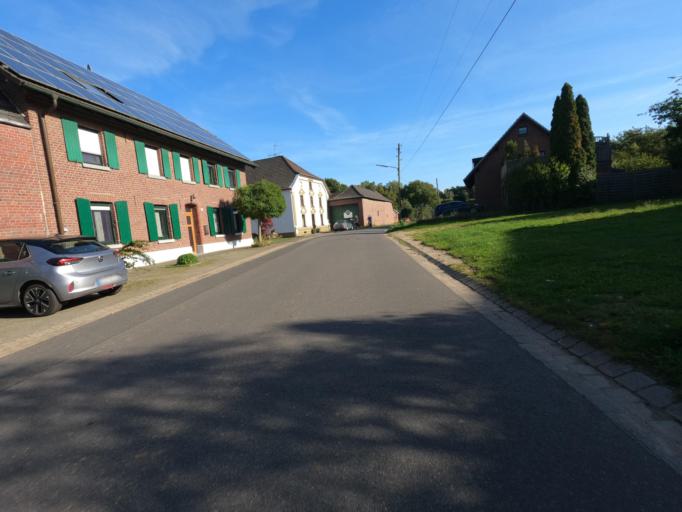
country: DE
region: North Rhine-Westphalia
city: Wegberg
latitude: 51.1760
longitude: 6.2758
